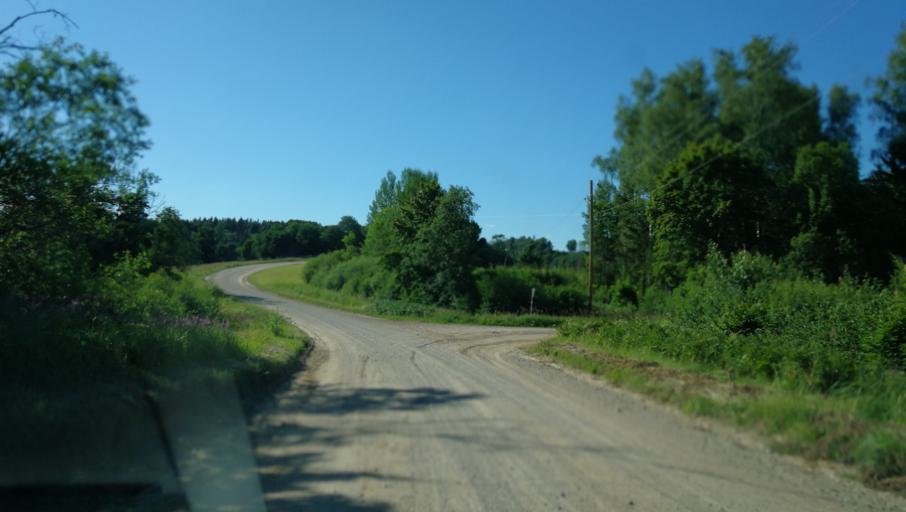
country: LV
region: Jaunpiebalga
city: Jaunpiebalga
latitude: 57.0246
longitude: 26.0298
